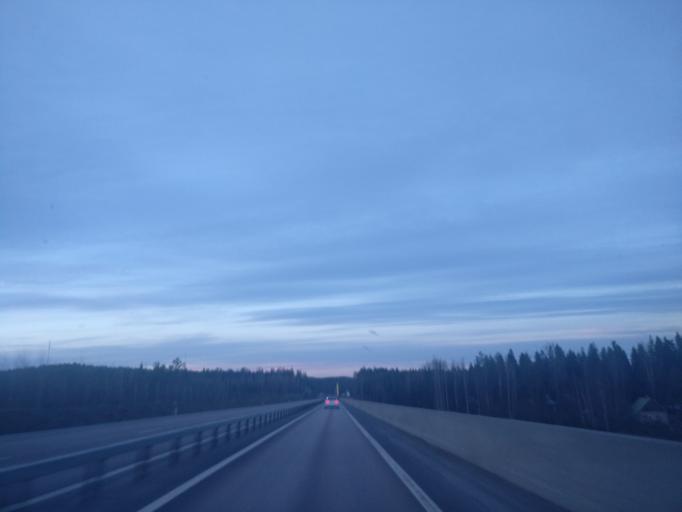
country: FI
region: Central Finland
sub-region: Jyvaeskylae
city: Saeynaetsalo
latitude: 62.2185
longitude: 25.8936
